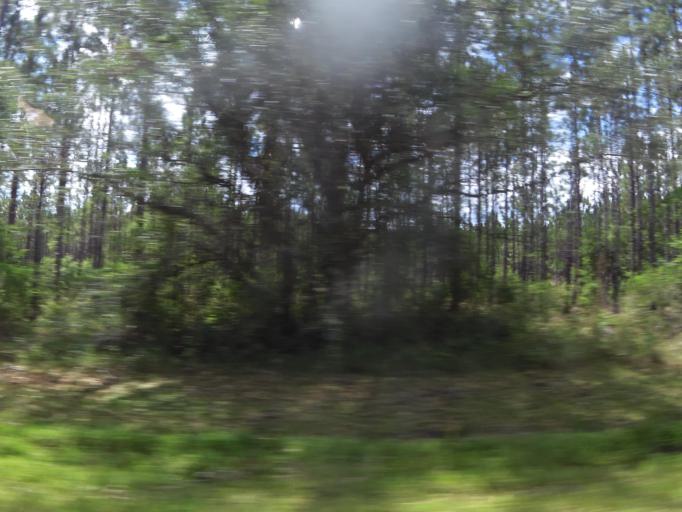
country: US
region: Florida
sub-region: Clay County
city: Green Cove Springs
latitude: 29.9342
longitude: -81.7509
